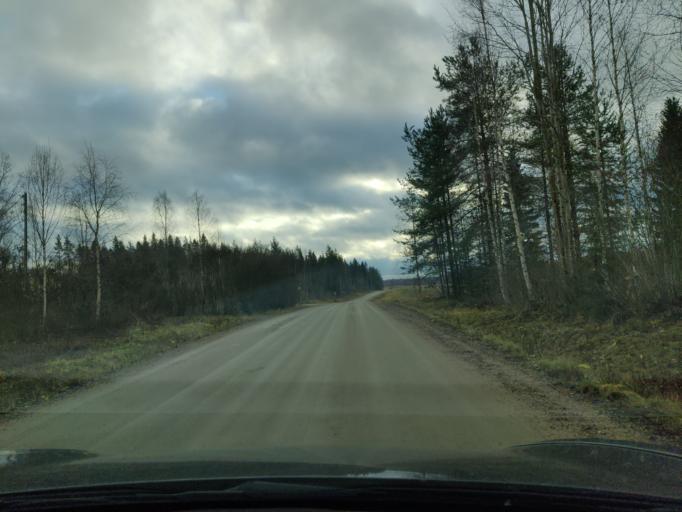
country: FI
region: Northern Savo
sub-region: Ylae-Savo
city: Kiuruvesi
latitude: 63.6385
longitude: 26.6346
